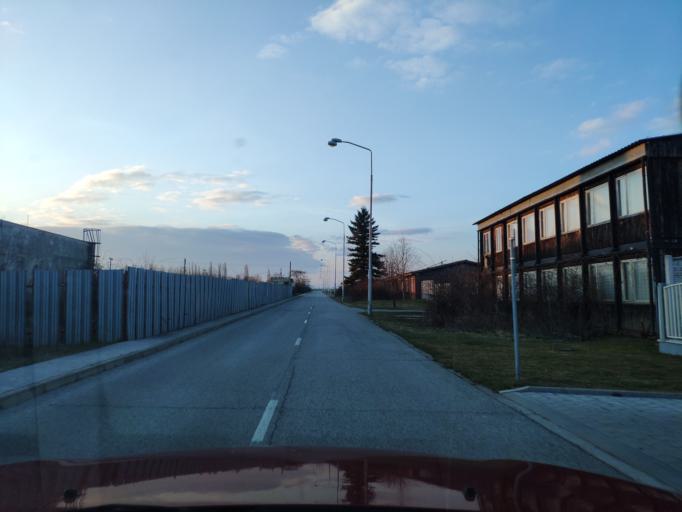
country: SK
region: Nitriansky
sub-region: Okres Nitra
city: Nitra
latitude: 48.2200
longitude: 18.0968
